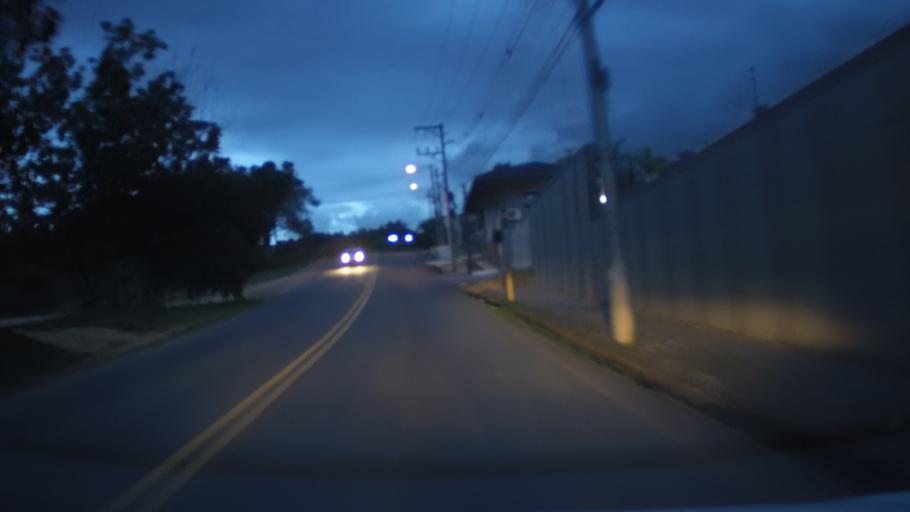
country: BR
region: Sao Paulo
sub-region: Vinhedo
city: Vinhedo
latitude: -23.0611
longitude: -47.0109
